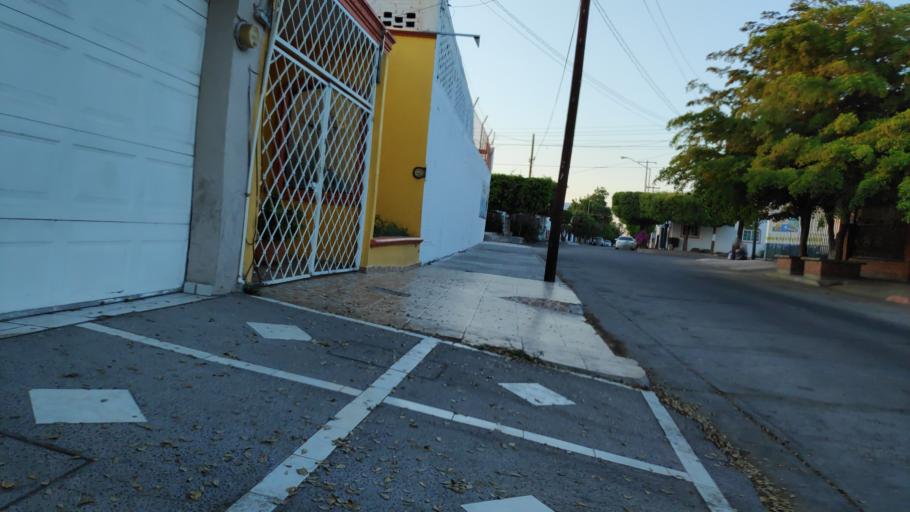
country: MX
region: Sinaloa
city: Culiacan
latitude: 24.7888
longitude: -107.4029
